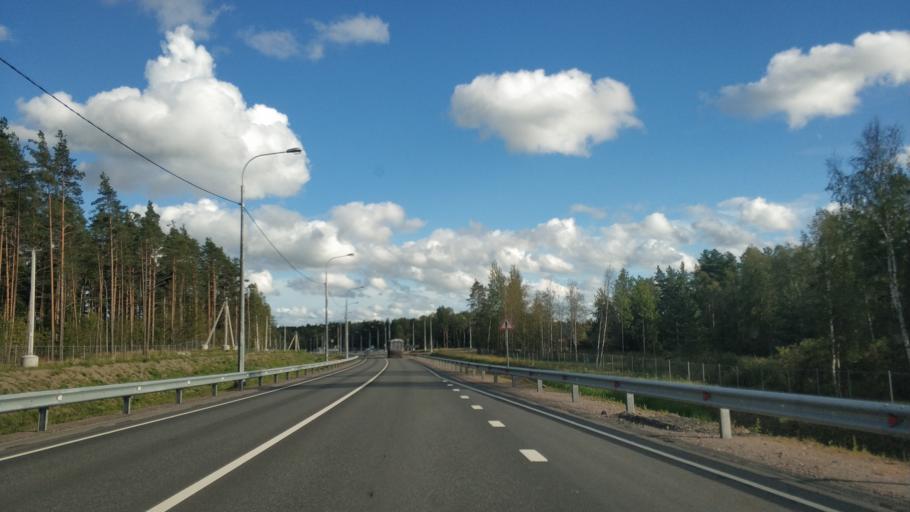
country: RU
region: Leningrad
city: Kuznechnoye
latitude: 61.1011
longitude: 29.9705
